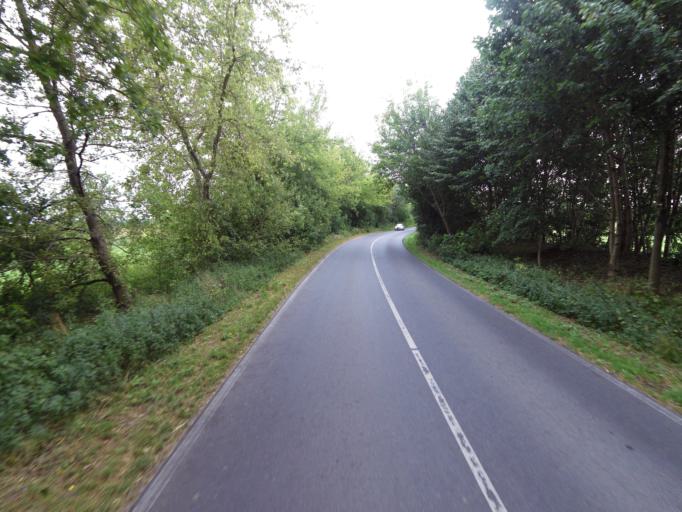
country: DE
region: Brandenburg
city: Zehdenick
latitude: 53.0192
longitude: 13.2877
